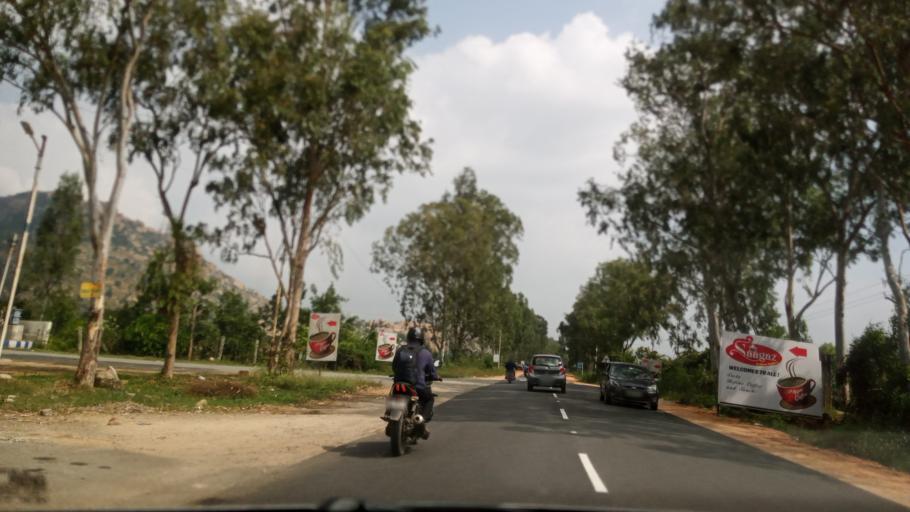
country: IN
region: Andhra Pradesh
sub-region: Chittoor
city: Madanapalle
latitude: 13.6360
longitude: 78.6005
